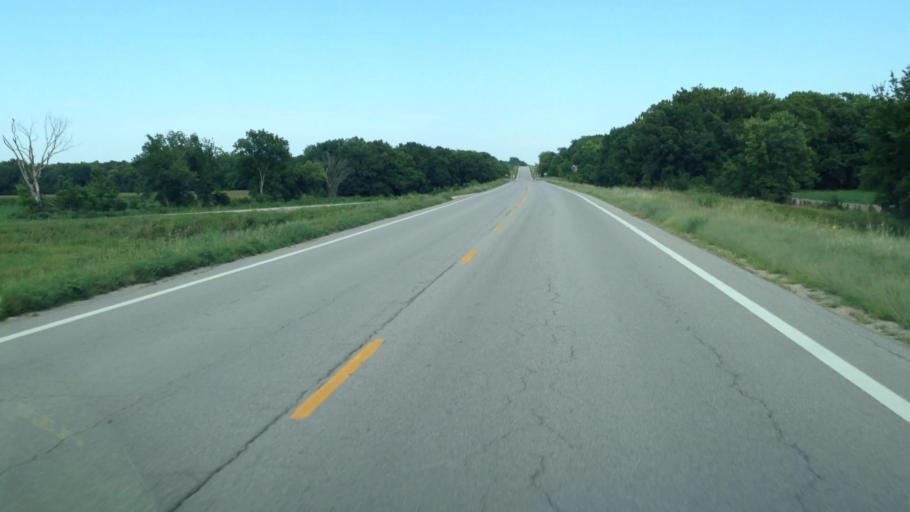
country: US
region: Kansas
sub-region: Neosho County
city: Erie
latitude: 37.6881
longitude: -95.2026
